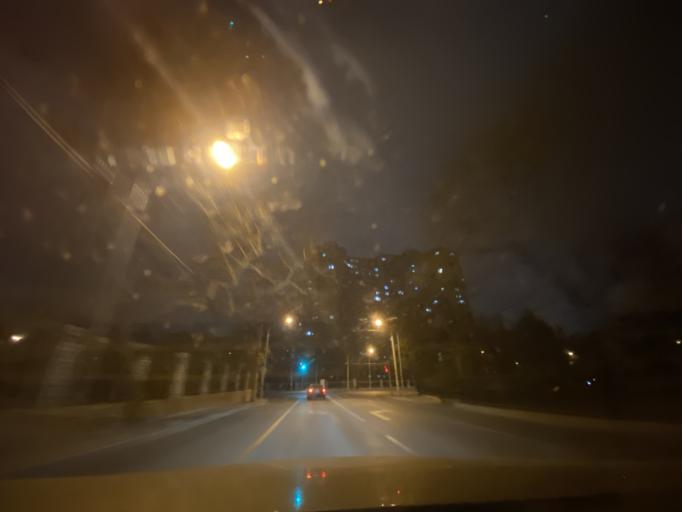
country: CN
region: Beijing
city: Jinrongjie
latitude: 39.8992
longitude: 116.3435
